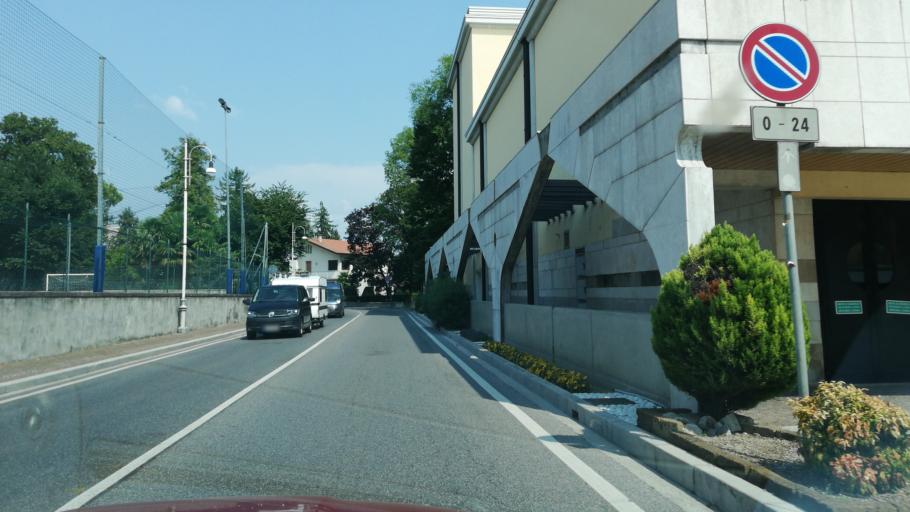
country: IT
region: Veneto
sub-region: Provincia di Venezia
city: San Michele al Tagliamento
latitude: 45.7765
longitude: 12.9966
